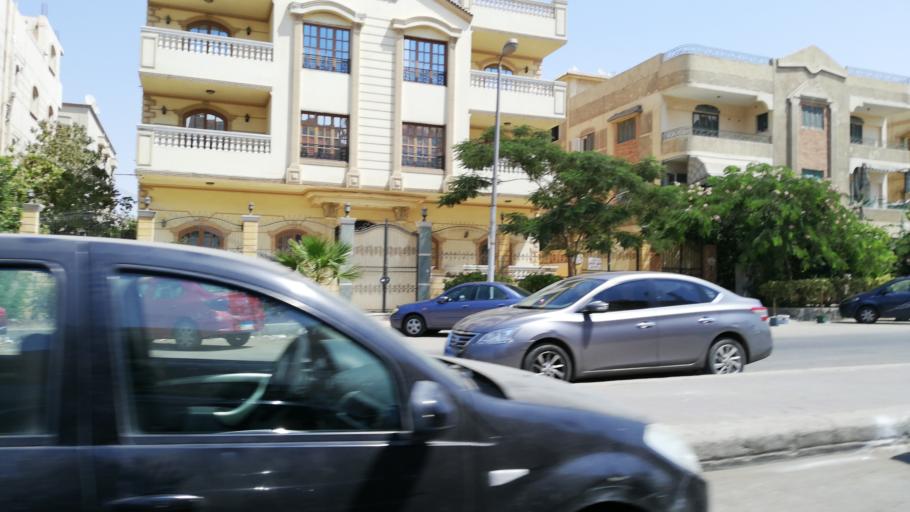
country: EG
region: Muhafazat al Qahirah
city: Cairo
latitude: 30.0047
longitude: 31.4391
